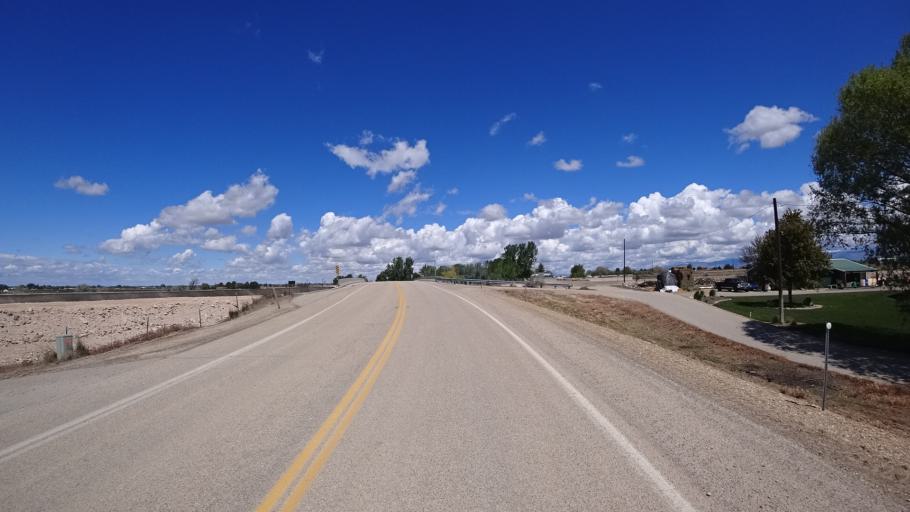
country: US
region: Idaho
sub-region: Ada County
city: Kuna
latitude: 43.4853
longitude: -116.3544
